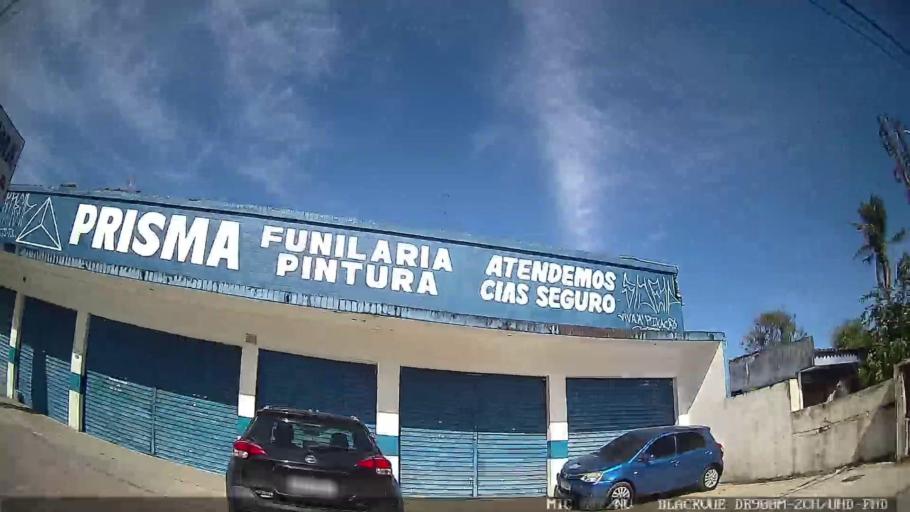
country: BR
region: Sao Paulo
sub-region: Guaruja
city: Guaruja
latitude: -23.9918
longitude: -46.2701
